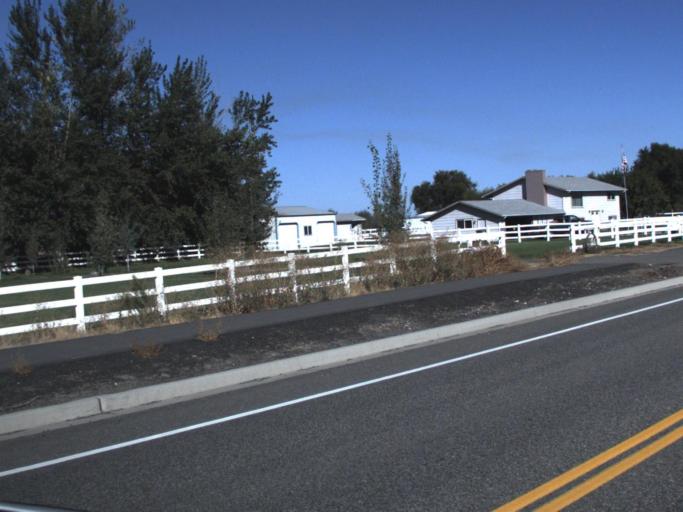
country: US
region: Washington
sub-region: Benton County
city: Finley
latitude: 46.1390
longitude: -119.0226
